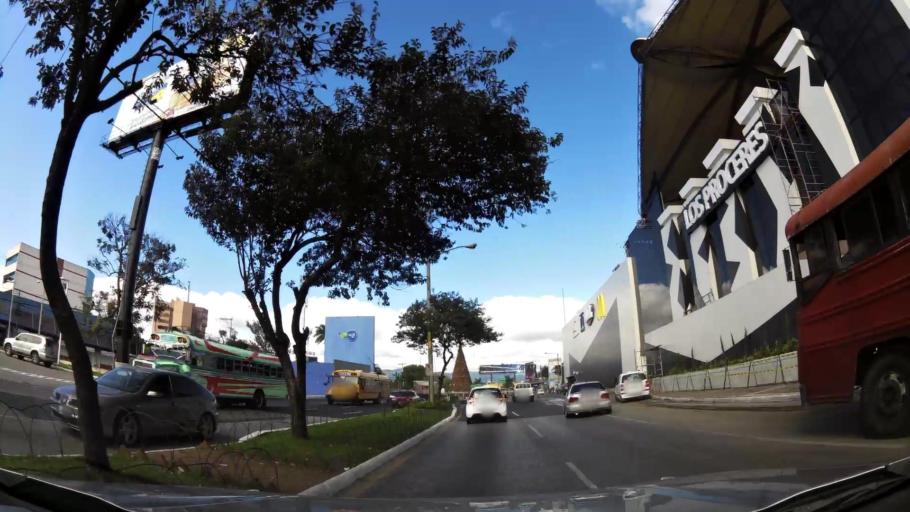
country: GT
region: Guatemala
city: Santa Catarina Pinula
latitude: 14.5940
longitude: -90.5154
